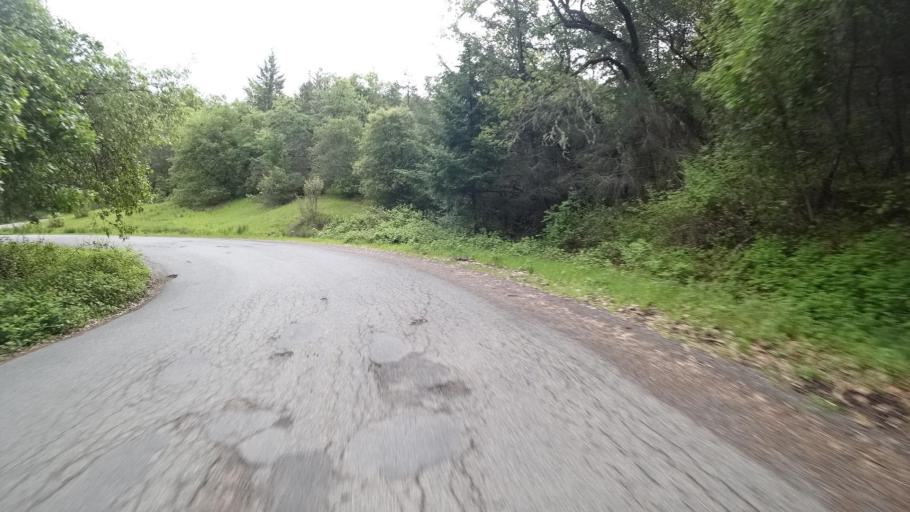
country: US
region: California
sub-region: Humboldt County
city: Redway
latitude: 40.1841
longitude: -123.5805
